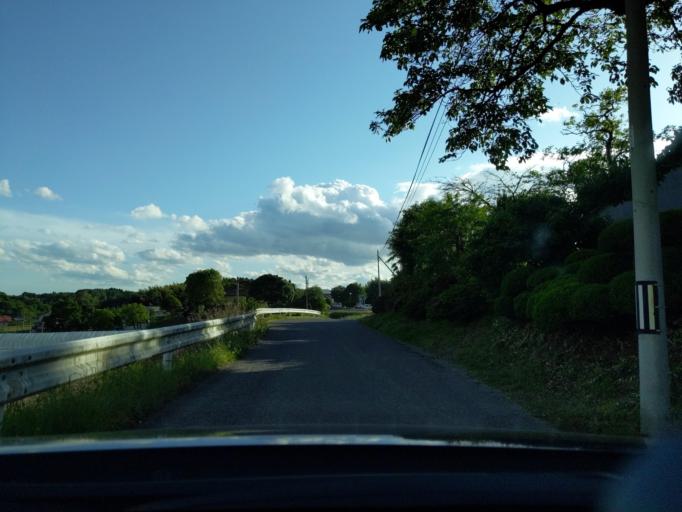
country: JP
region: Fukushima
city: Miharu
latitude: 37.4246
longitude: 140.4620
